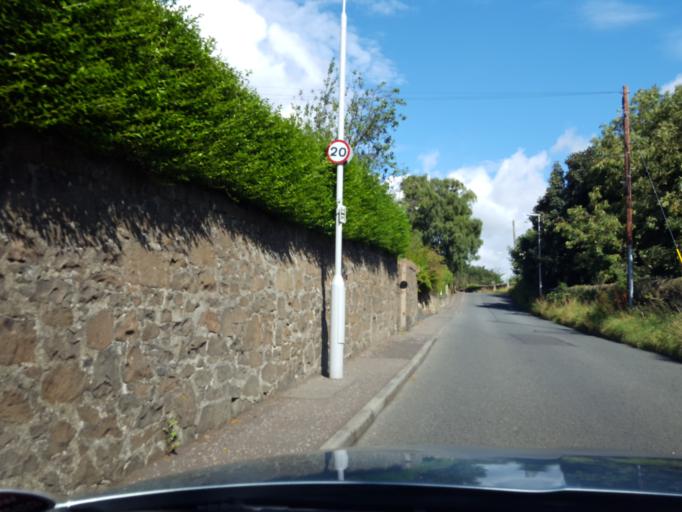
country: GB
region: Scotland
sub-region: Fife
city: North Queensferry
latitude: 56.0135
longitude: -3.3934
